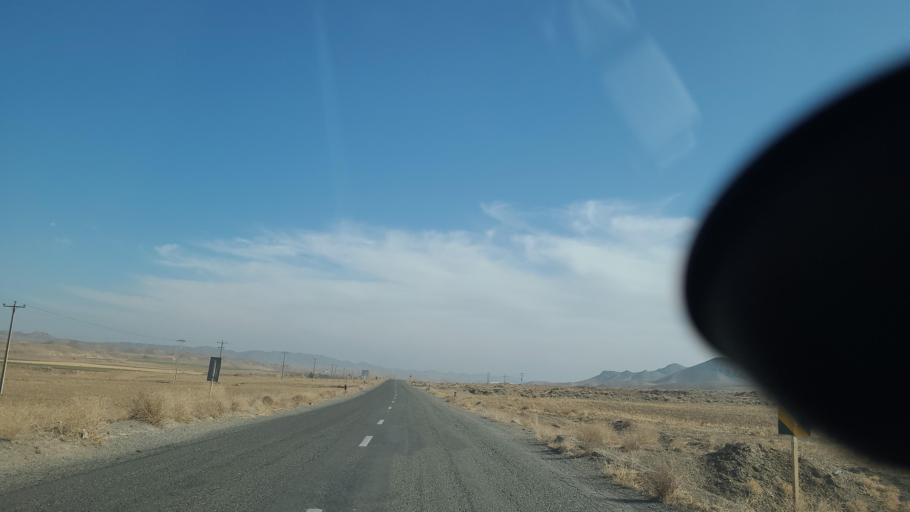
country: IR
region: Razavi Khorasan
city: Fariman
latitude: 35.5874
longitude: 59.6515
